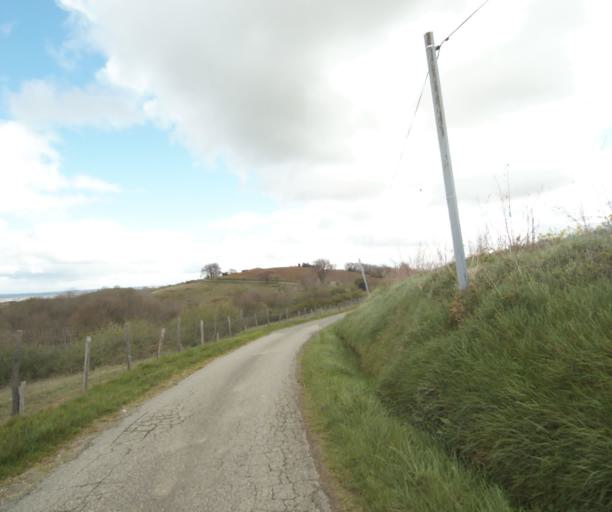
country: FR
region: Midi-Pyrenees
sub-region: Departement de l'Ariege
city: Saverdun
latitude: 43.2010
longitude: 1.5561
